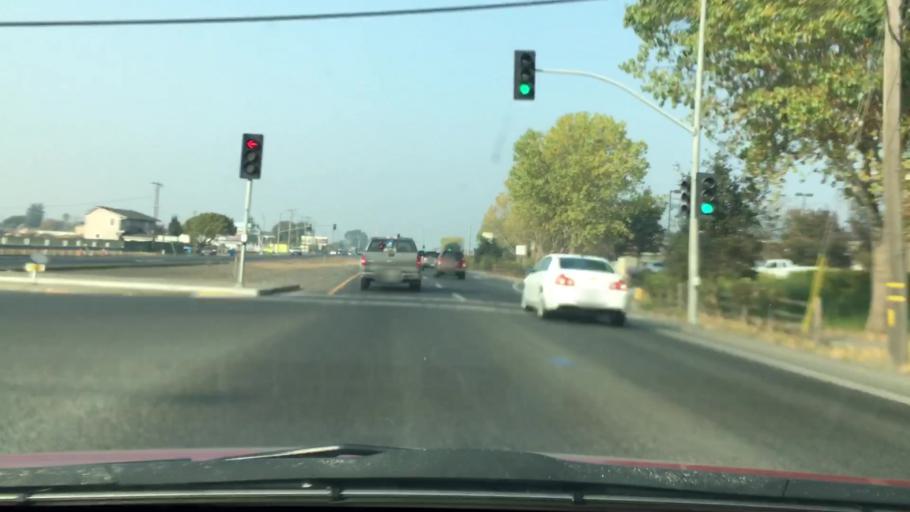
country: US
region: California
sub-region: Napa County
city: American Canyon
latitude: 38.1792
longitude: -122.2546
